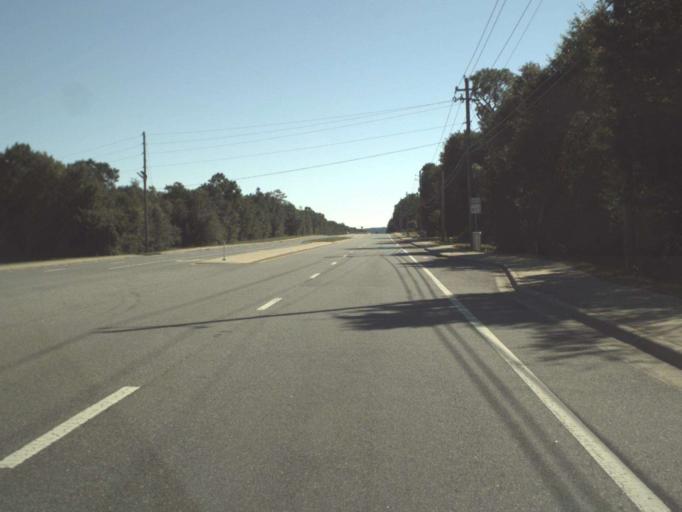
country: US
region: Florida
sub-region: Santa Rosa County
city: East Milton
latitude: 30.6153
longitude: -86.9606
